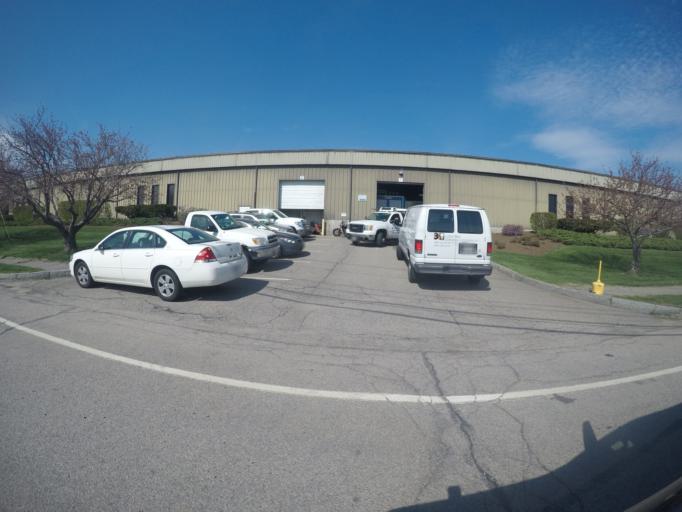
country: US
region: Massachusetts
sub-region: Bristol County
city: Easton
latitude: 42.0476
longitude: -71.0736
